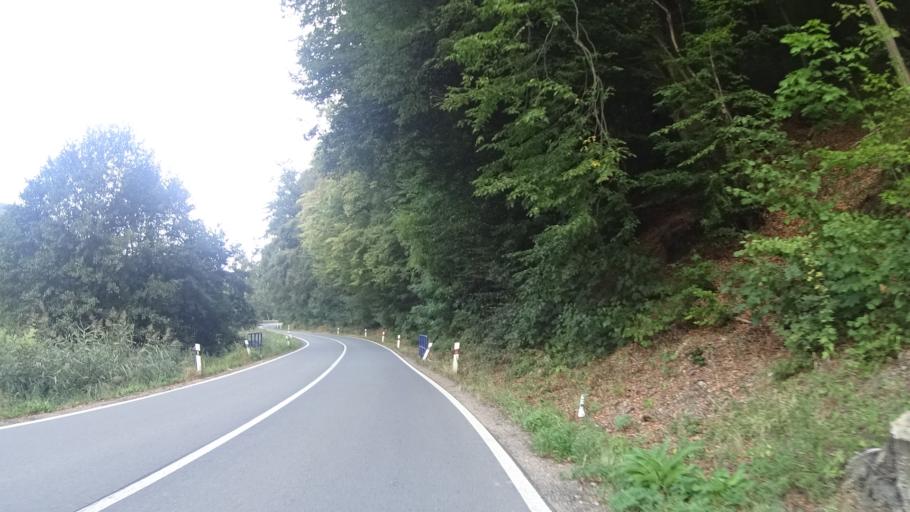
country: CZ
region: Olomoucky
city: Stity
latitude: 49.8679
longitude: 16.7511
